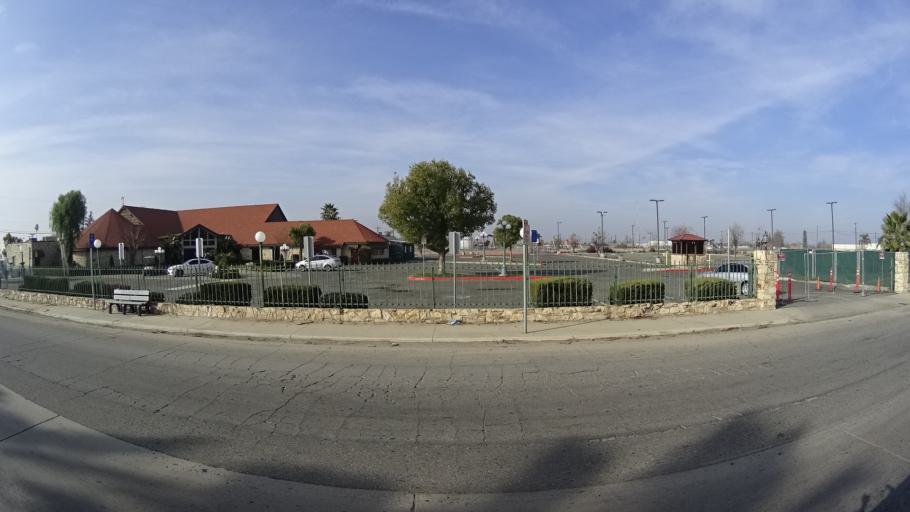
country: US
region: California
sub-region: Kern County
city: Bakersfield
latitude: 35.3456
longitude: -119.0031
